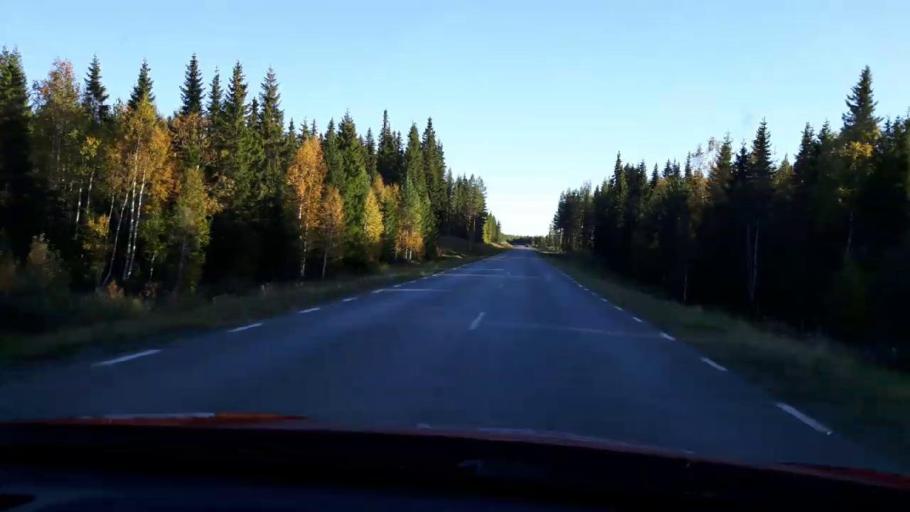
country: SE
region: Jaemtland
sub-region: OEstersunds Kommun
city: Lit
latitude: 63.7857
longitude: 14.7049
